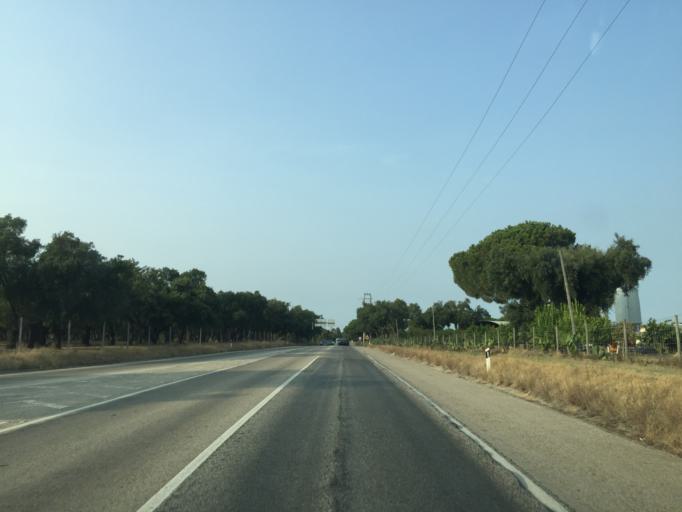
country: PT
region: Setubal
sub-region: Setubal
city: Setubal
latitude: 38.5822
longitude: -8.6803
